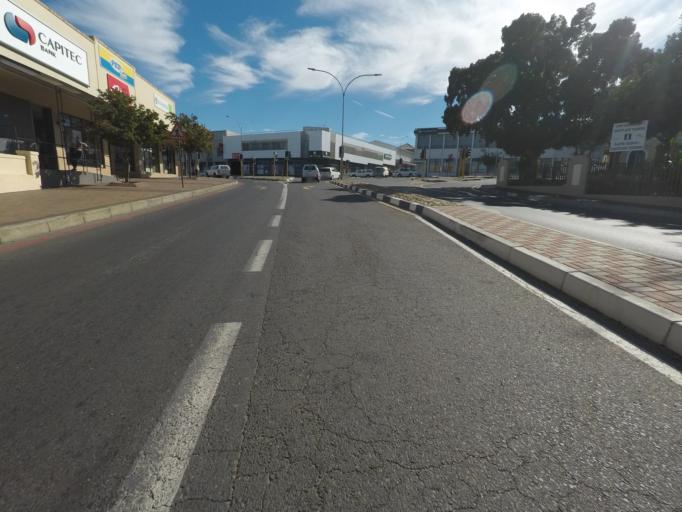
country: ZA
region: Western Cape
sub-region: West Coast District Municipality
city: Malmesbury
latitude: -33.4628
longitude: 18.7295
